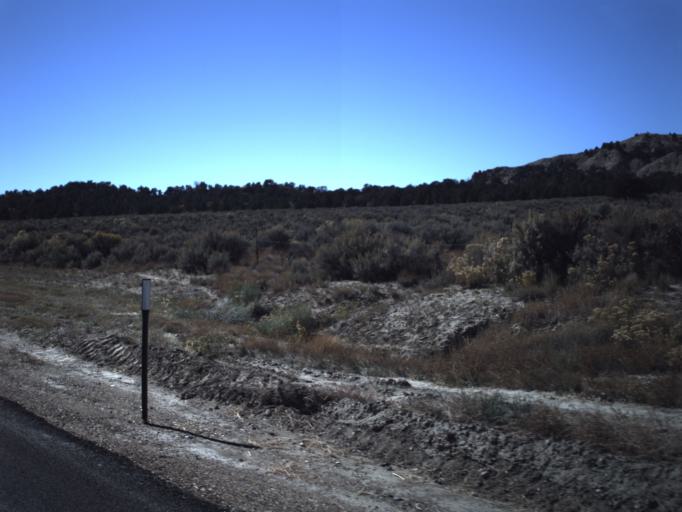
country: US
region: Utah
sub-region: Garfield County
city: Panguitch
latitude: 37.6509
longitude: -111.8422
